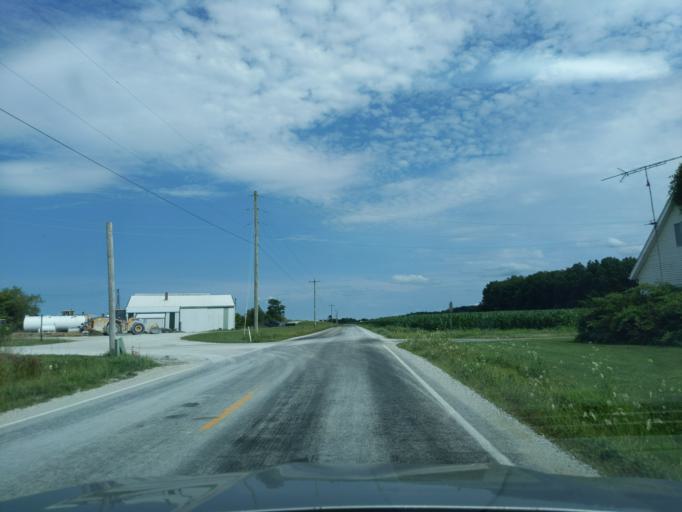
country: US
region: Indiana
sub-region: Ripley County
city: Osgood
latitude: 39.2030
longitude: -85.3158
